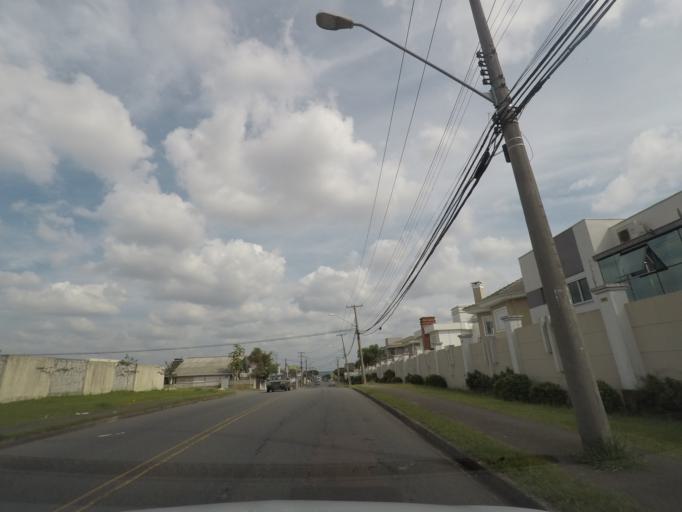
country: BR
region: Parana
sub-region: Sao Jose Dos Pinhais
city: Sao Jose dos Pinhais
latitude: -25.4869
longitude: -49.2136
